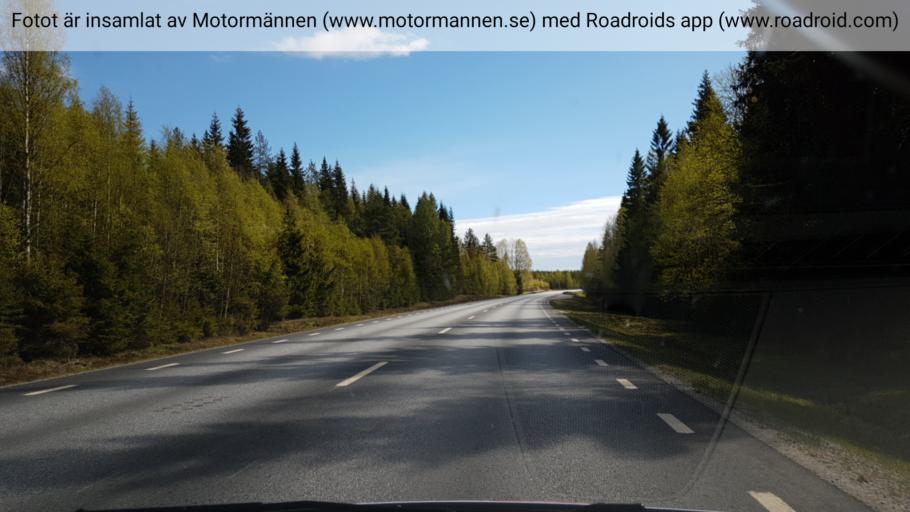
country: SE
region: Vaesterbotten
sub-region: Vannas Kommun
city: Vannasby
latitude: 64.0740
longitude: 19.9896
